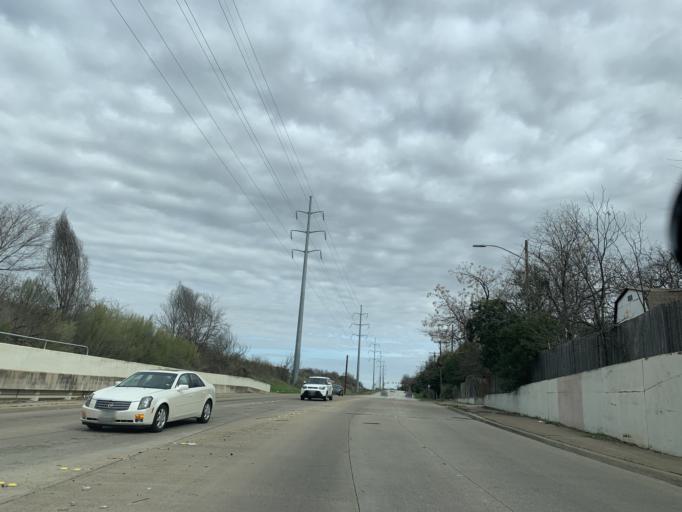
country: US
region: Texas
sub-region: Tarrant County
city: Edgecliff Village
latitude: 32.6755
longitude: -97.3803
